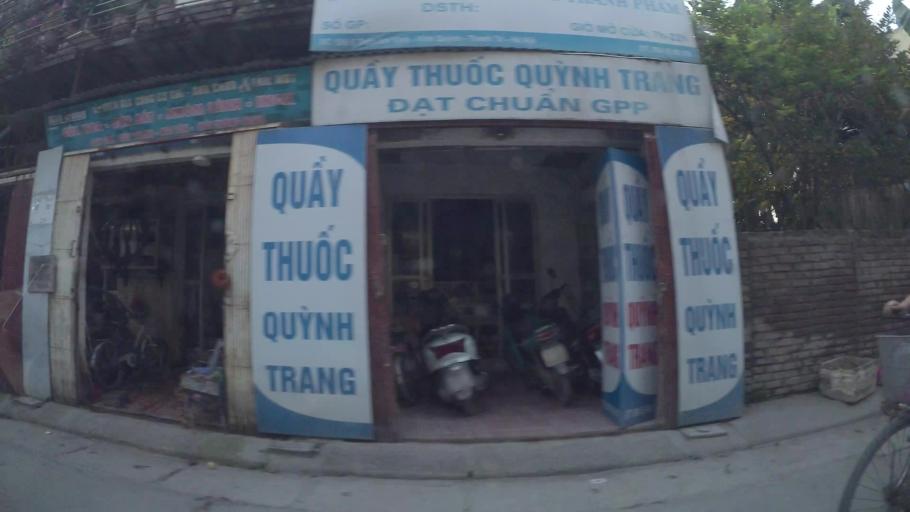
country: VN
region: Ha Noi
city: Van Dien
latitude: 20.9323
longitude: 105.8357
